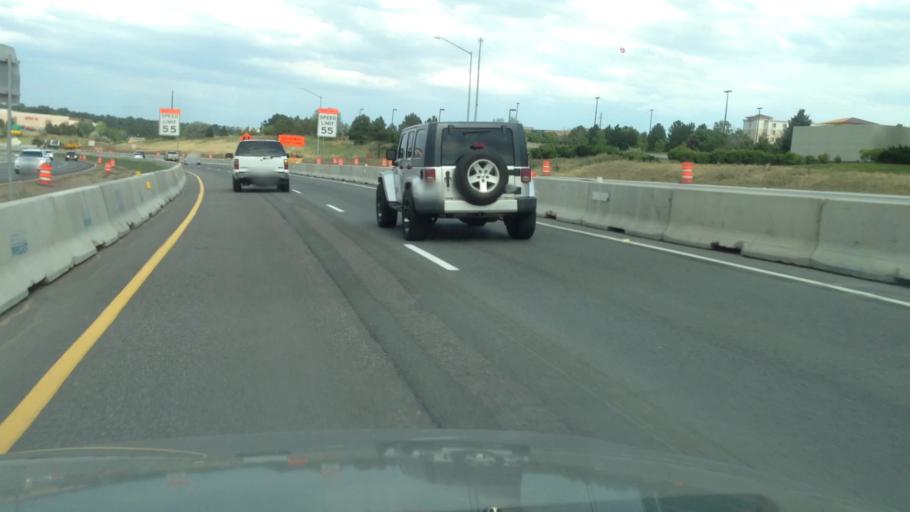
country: US
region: Colorado
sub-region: Douglas County
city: Highlands Ranch
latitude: 39.5587
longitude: -105.0027
